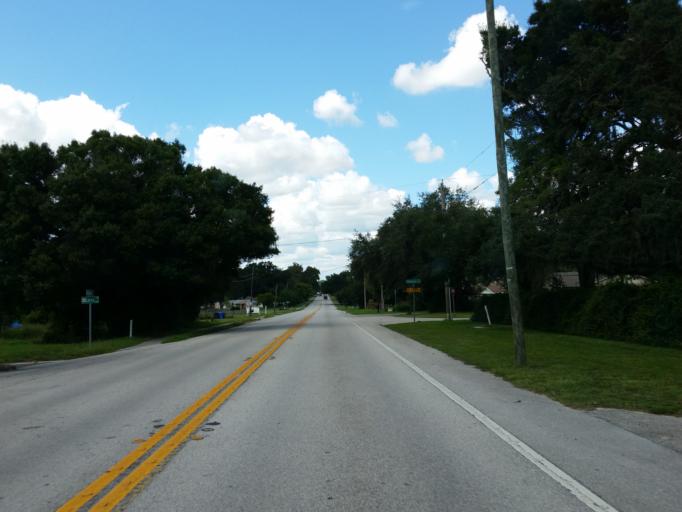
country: US
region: Florida
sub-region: Hillsborough County
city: Bloomingdale
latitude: 27.9117
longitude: -82.2597
